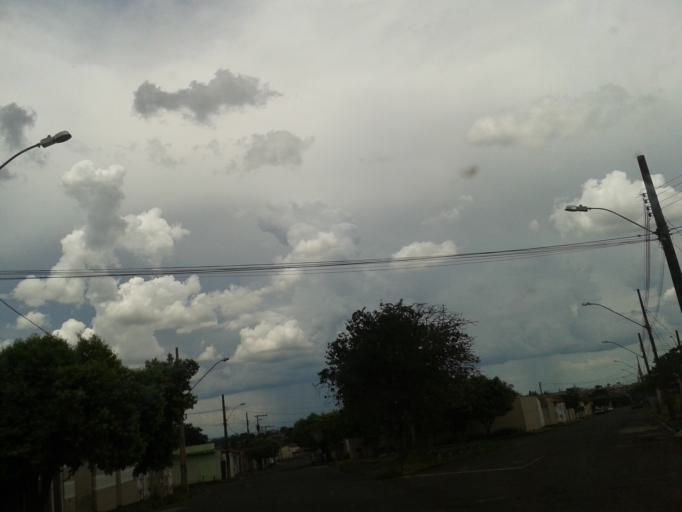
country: BR
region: Minas Gerais
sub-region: Ituiutaba
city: Ituiutaba
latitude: -18.9874
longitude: -49.4531
